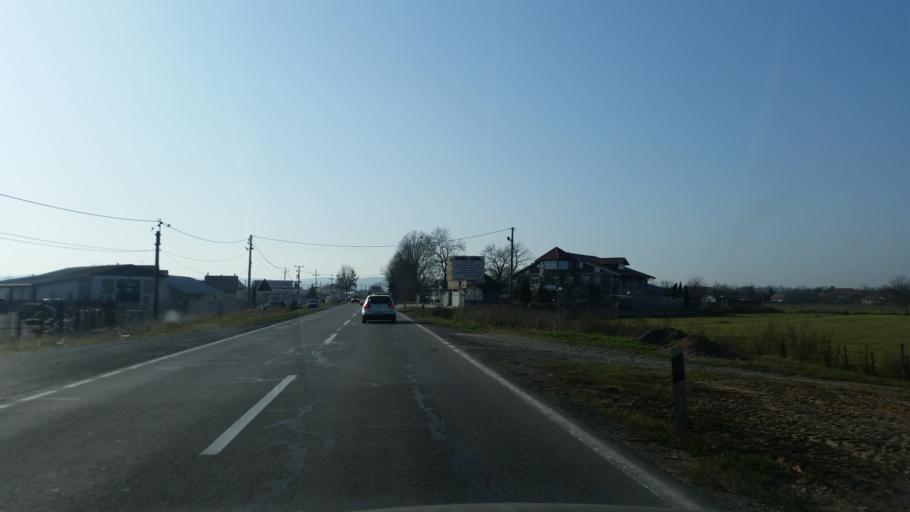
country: RS
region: Central Serbia
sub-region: Belgrade
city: Lazarevac
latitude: 44.4061
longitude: 20.2517
